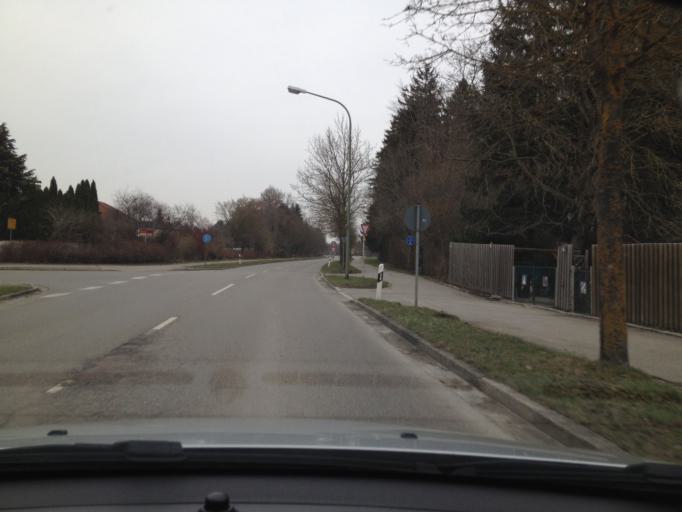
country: DE
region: Bavaria
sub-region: Swabia
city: Wehringen
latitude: 48.2719
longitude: 10.8015
